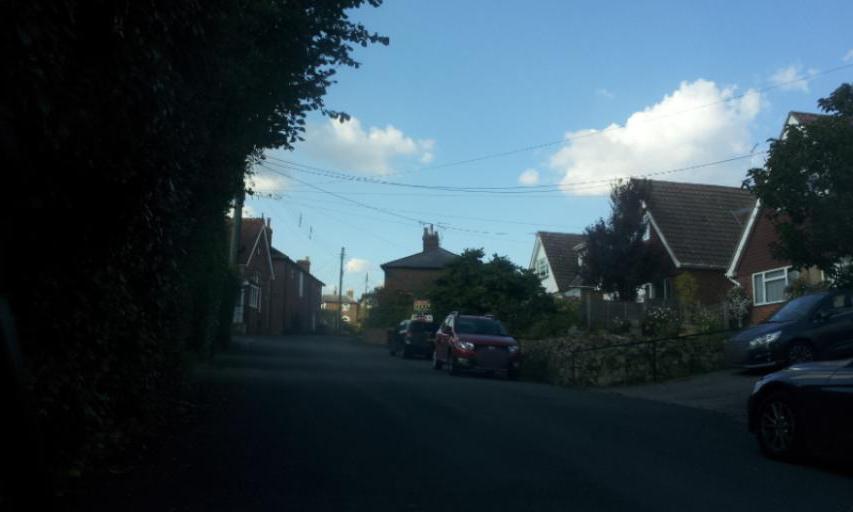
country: GB
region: England
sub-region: Kent
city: Kings Hill
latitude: 51.2644
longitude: 0.3776
